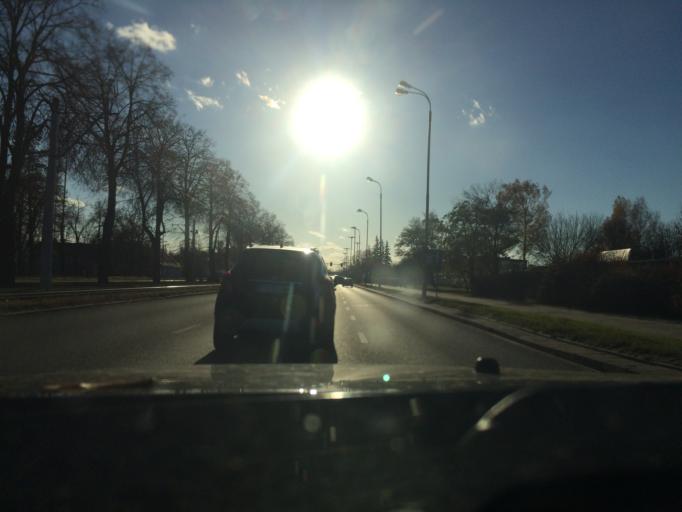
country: PL
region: Lodz Voivodeship
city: Lodz
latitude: 51.7208
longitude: 19.4398
